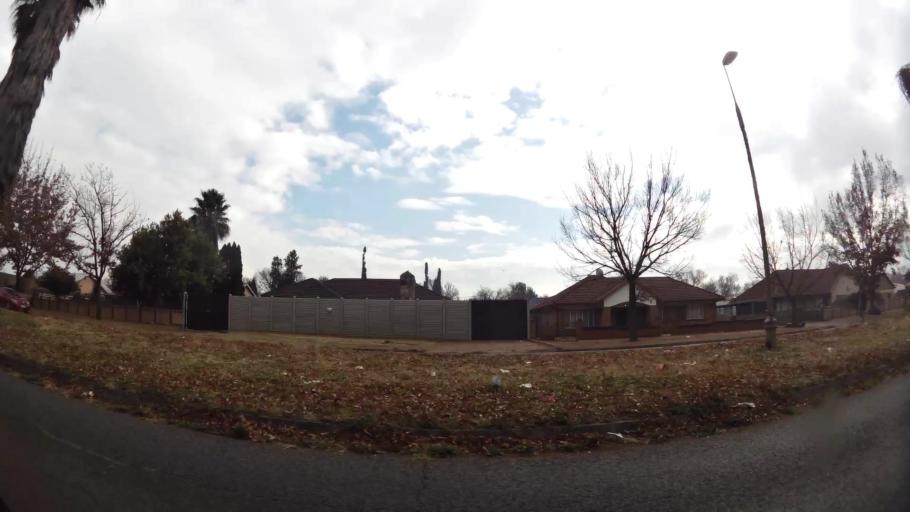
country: ZA
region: Gauteng
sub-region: Sedibeng District Municipality
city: Vanderbijlpark
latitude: -26.6969
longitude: 27.8449
